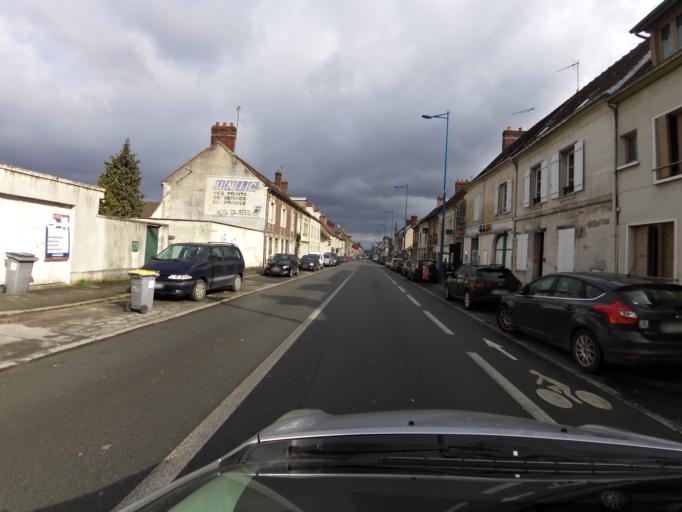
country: FR
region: Picardie
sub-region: Departement de l'Oise
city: Pont-Sainte-Maxence
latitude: 49.2978
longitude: 2.6046
